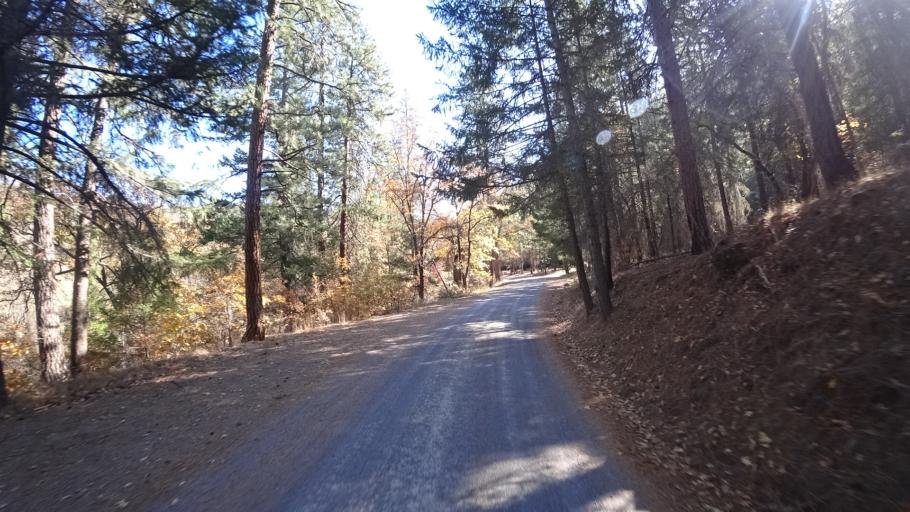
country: US
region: California
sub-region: Siskiyou County
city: Yreka
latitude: 41.8548
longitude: -122.7024
